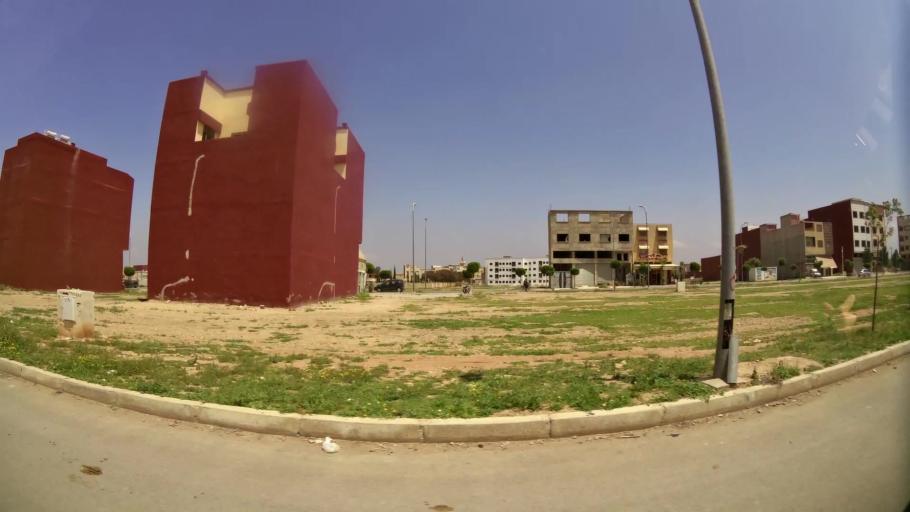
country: MA
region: Oriental
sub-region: Oujda-Angad
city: Oujda
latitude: 34.6942
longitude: -1.8929
